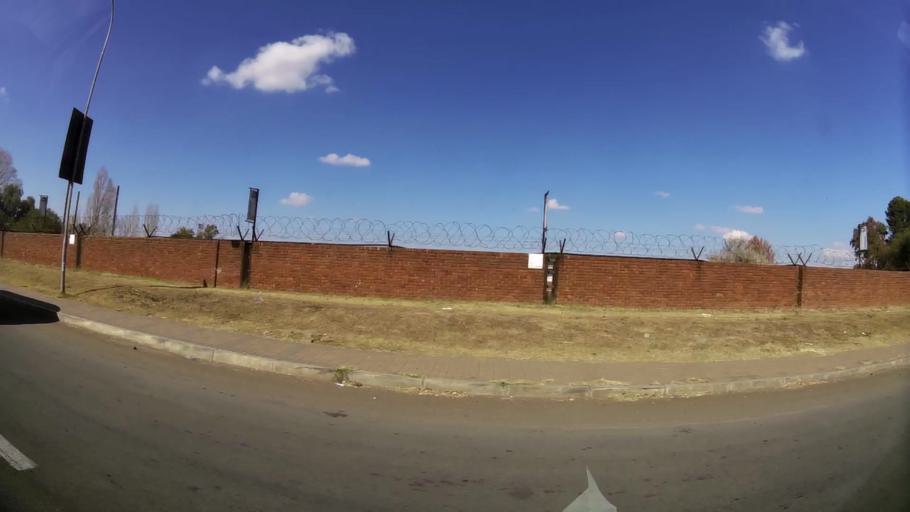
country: ZA
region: Orange Free State
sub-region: Mangaung Metropolitan Municipality
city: Bloemfontein
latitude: -29.1184
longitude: 26.2350
